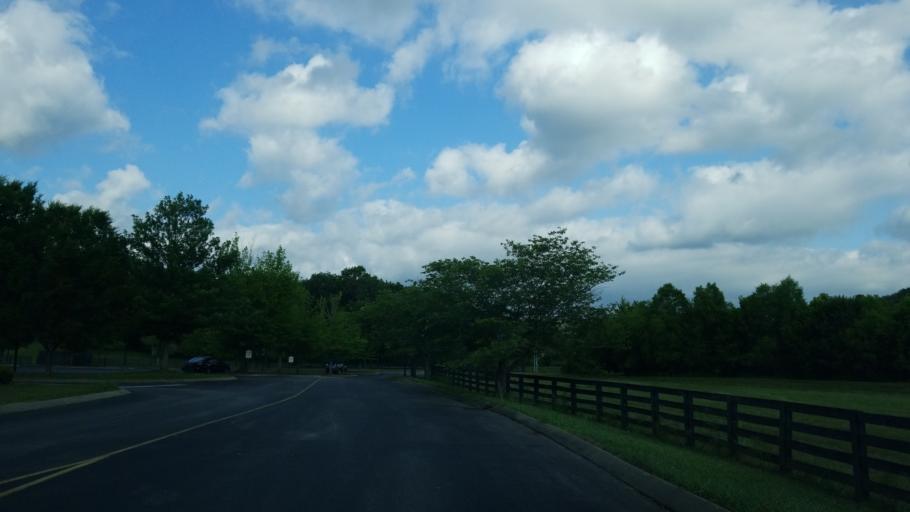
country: US
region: Tennessee
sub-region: Davidson County
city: Forest Hills
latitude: 36.0303
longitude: -86.8583
